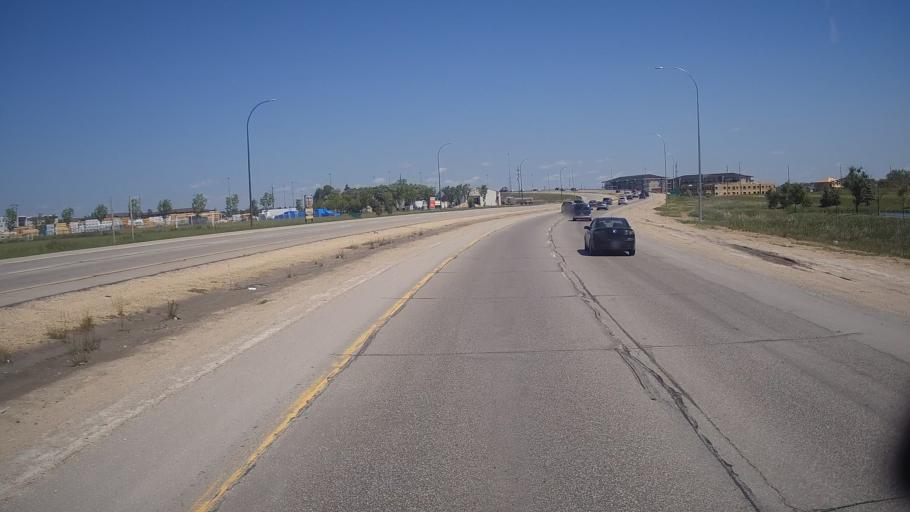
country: CA
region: Manitoba
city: Winnipeg
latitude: 49.9062
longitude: -97.0630
